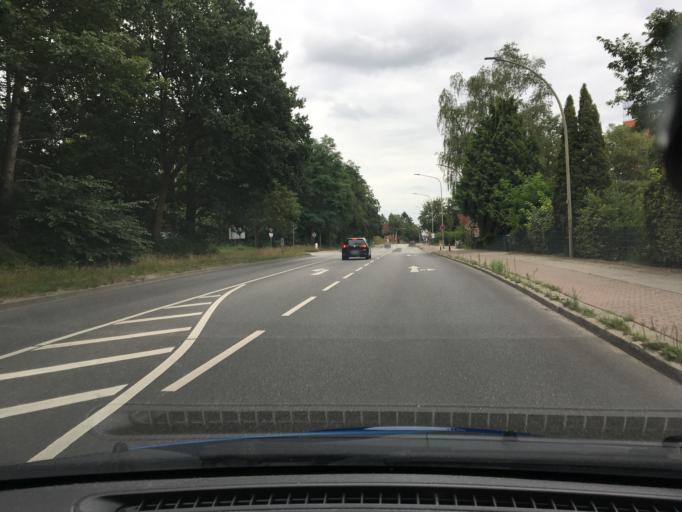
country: DE
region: Schleswig-Holstein
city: Geesthacht
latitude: 53.4518
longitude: 10.3571
